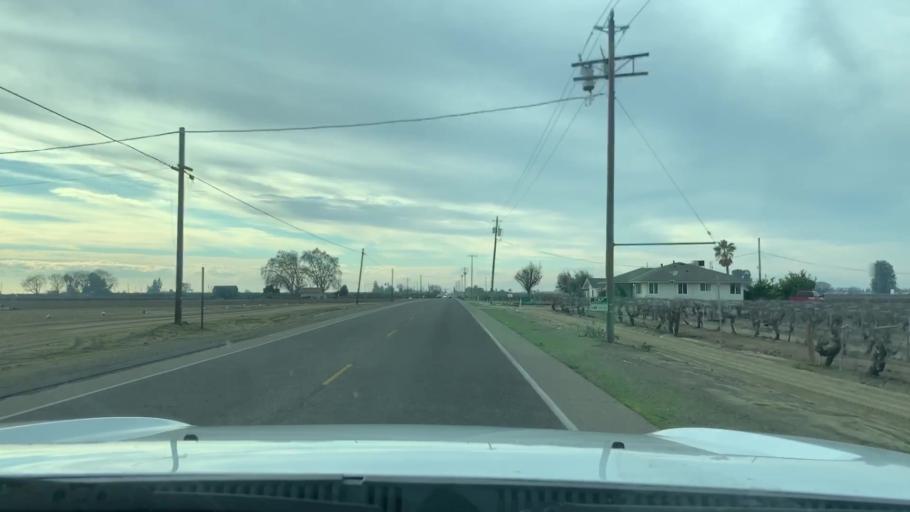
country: US
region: California
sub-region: Fresno County
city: Easton
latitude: 36.6053
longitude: -119.7743
